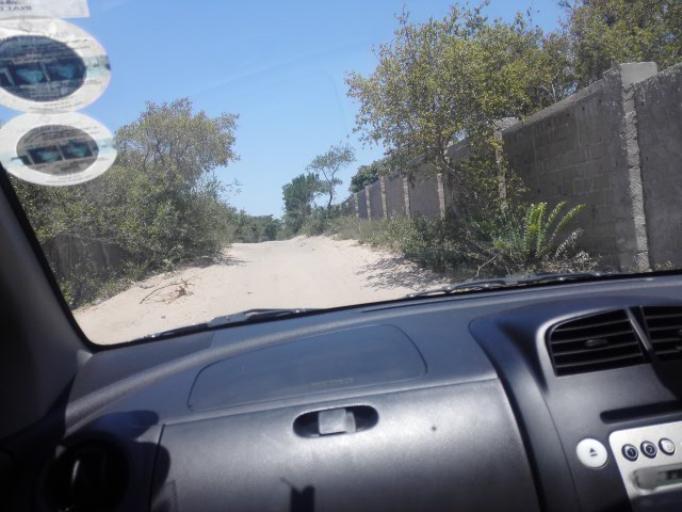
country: MZ
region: Maputo City
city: Maputo
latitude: -25.7390
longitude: 32.7355
